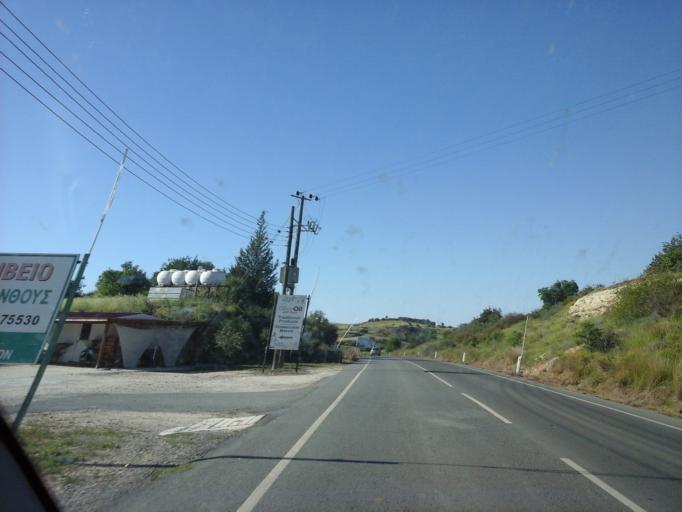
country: CY
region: Pafos
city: Polis
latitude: 35.0007
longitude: 32.4445
